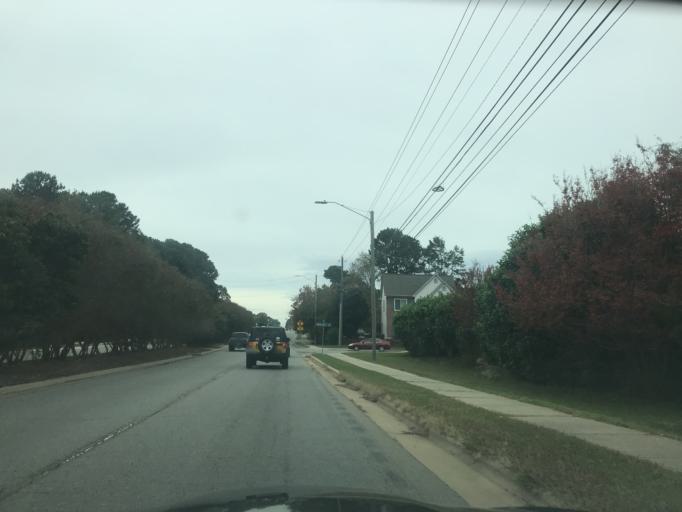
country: US
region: North Carolina
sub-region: Wake County
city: West Raleigh
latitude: 35.8804
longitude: -78.6787
